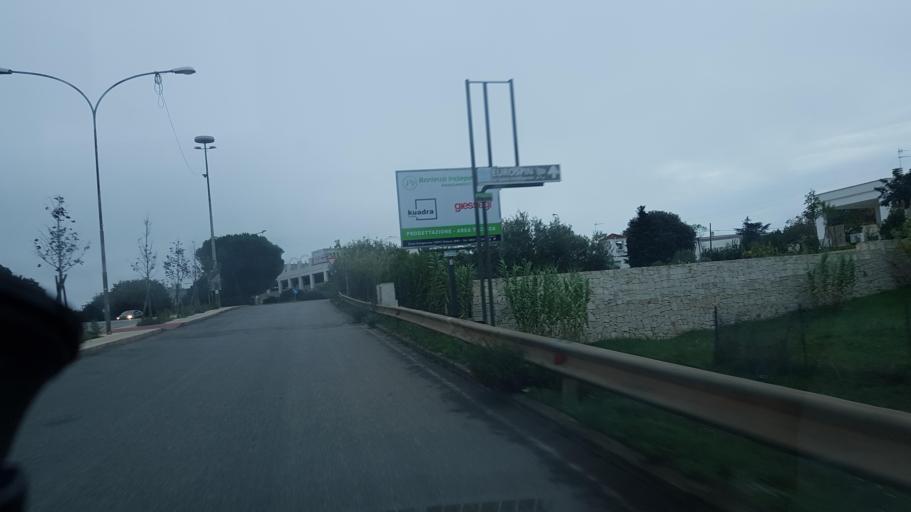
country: IT
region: Apulia
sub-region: Provincia di Brindisi
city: Ostuni
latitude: 40.7246
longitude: 17.5716
